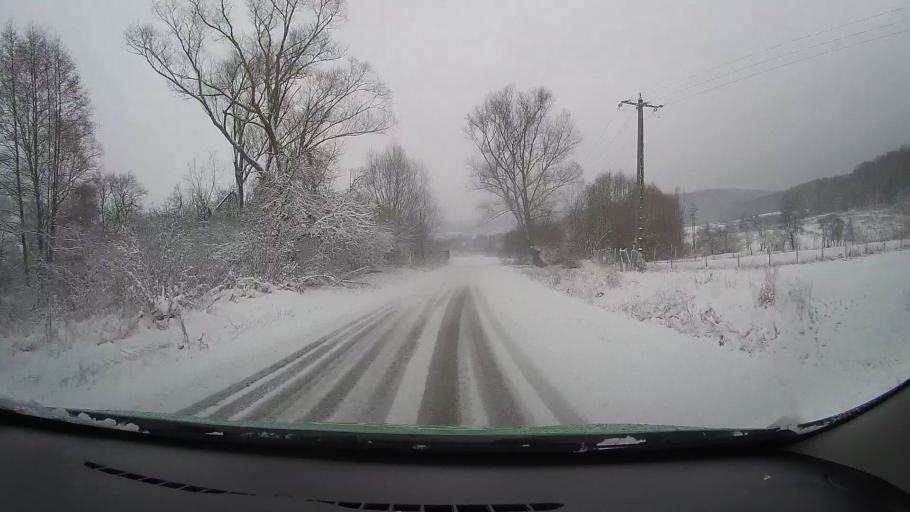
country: RO
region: Hunedoara
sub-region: Comuna Carjiti
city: Carjiti
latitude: 45.8347
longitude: 22.8401
